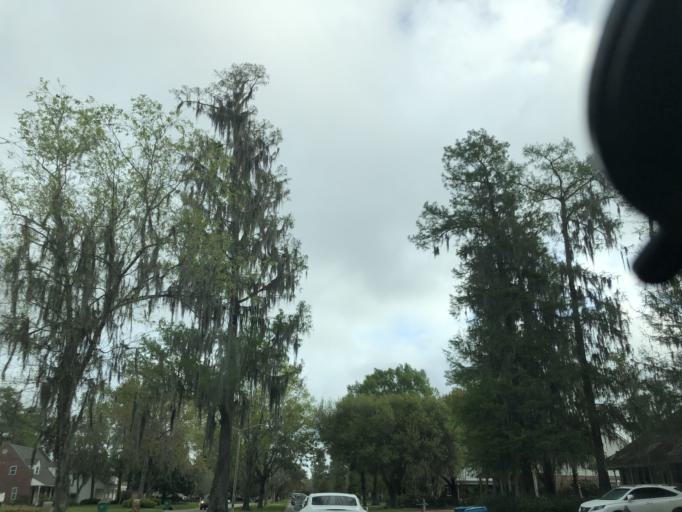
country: US
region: Louisiana
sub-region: Saint Charles Parish
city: New Sarpy
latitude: 29.9753
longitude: -90.3648
